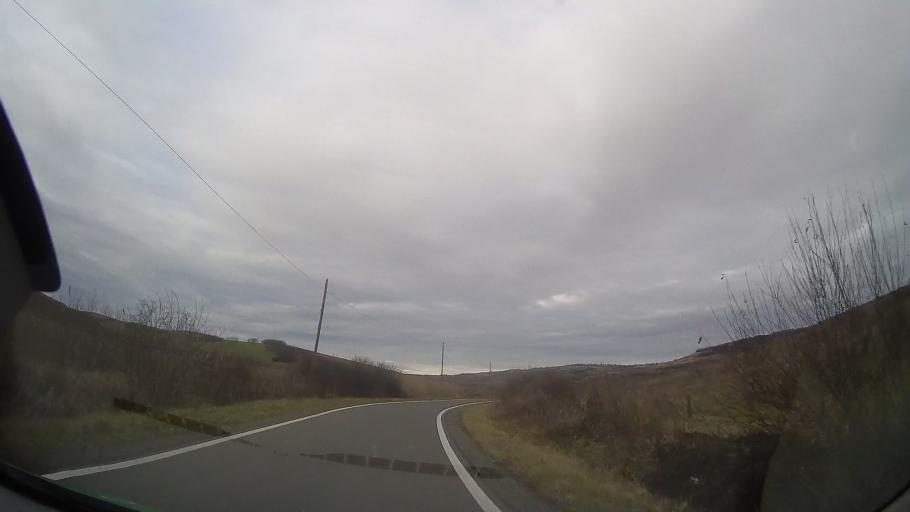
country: RO
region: Mures
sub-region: Comuna Cozma
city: Cozma
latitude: 46.7905
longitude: 24.5440
